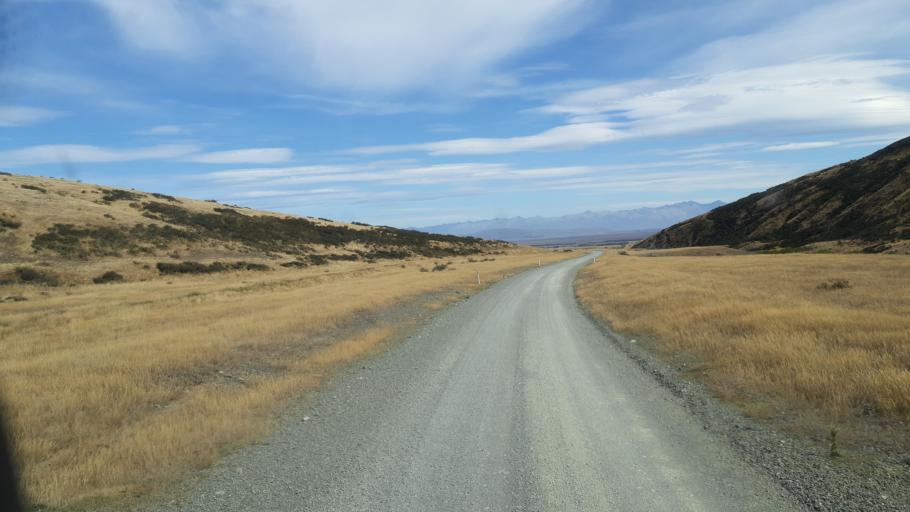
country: NZ
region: Canterbury
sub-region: Timaru District
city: Pleasant Point
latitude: -44.1948
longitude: 170.5756
